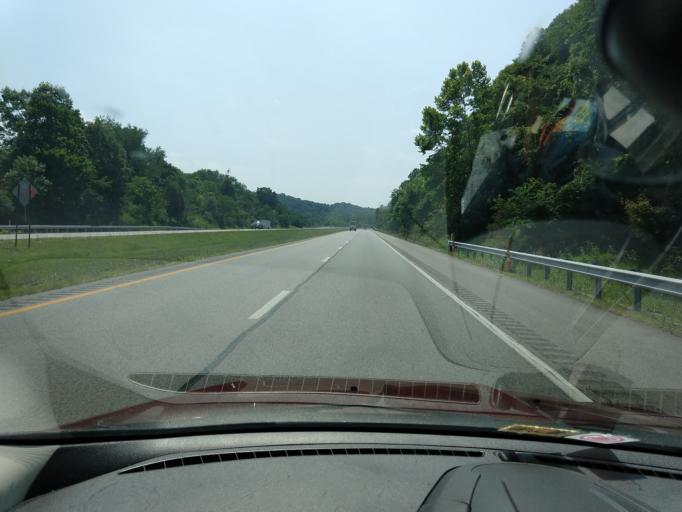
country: US
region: West Virginia
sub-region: Jackson County
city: Ripley
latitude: 38.7261
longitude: -81.6547
